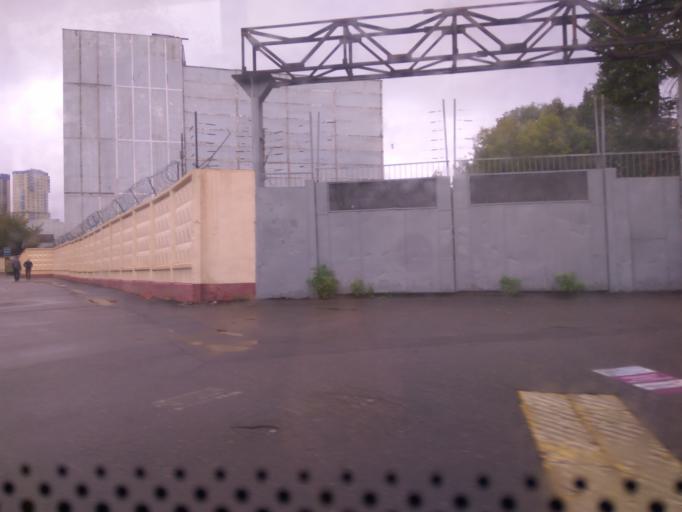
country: RU
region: Moscow
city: Lefortovo
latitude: 55.7852
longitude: 37.7221
